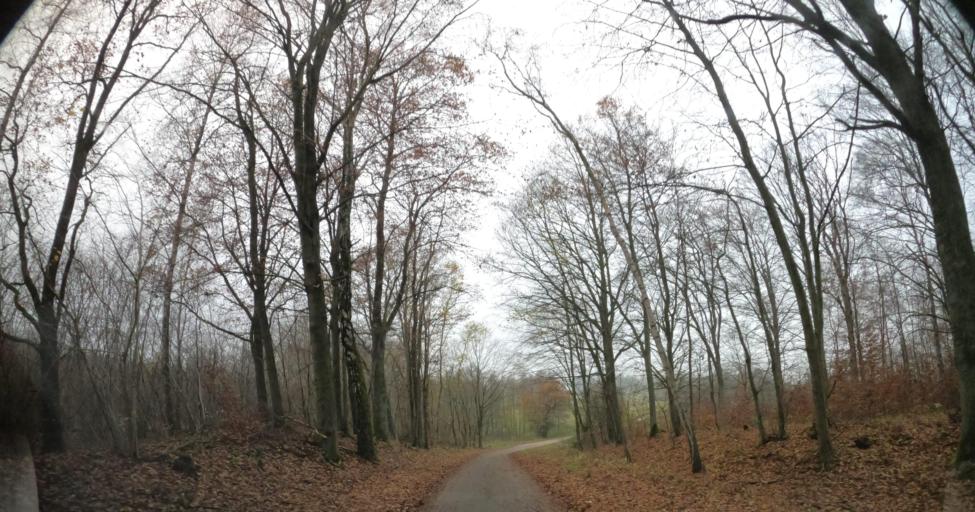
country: PL
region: West Pomeranian Voivodeship
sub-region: Powiat drawski
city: Drawsko Pomorskie
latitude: 53.5841
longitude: 15.8012
